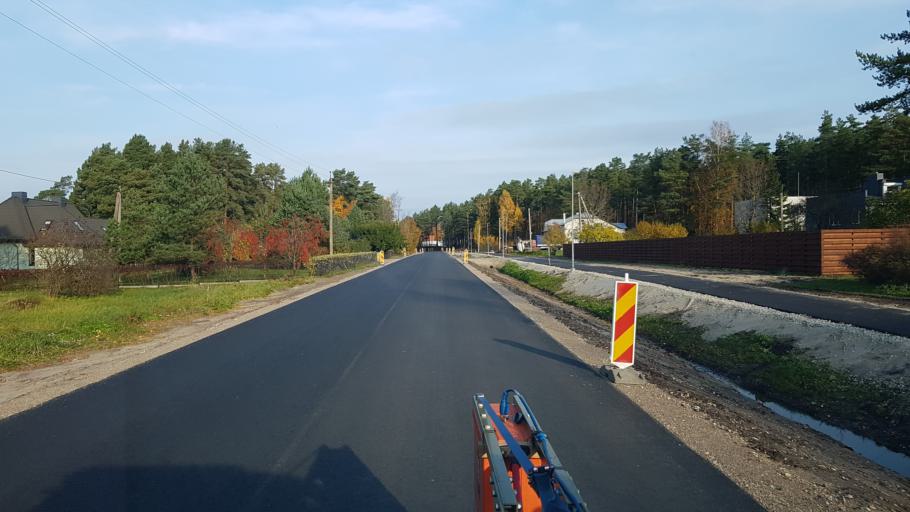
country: EE
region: Paernumaa
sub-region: Paikuse vald
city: Paikuse
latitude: 58.3515
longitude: 24.6199
